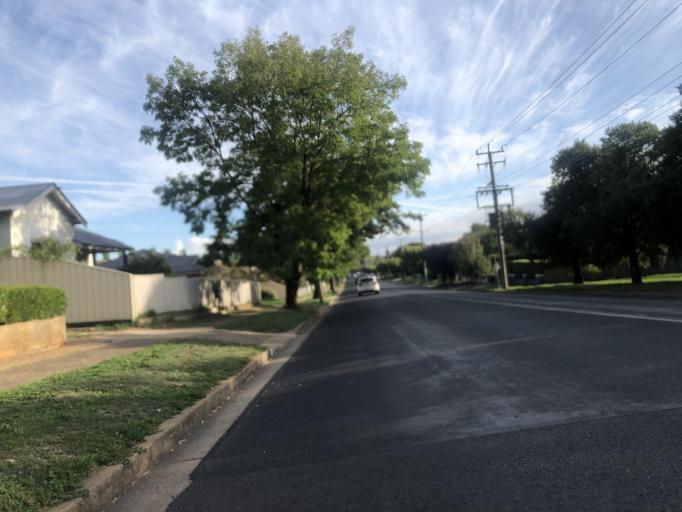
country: AU
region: New South Wales
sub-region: Orange Municipality
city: Orange
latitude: -33.2940
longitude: 149.0966
